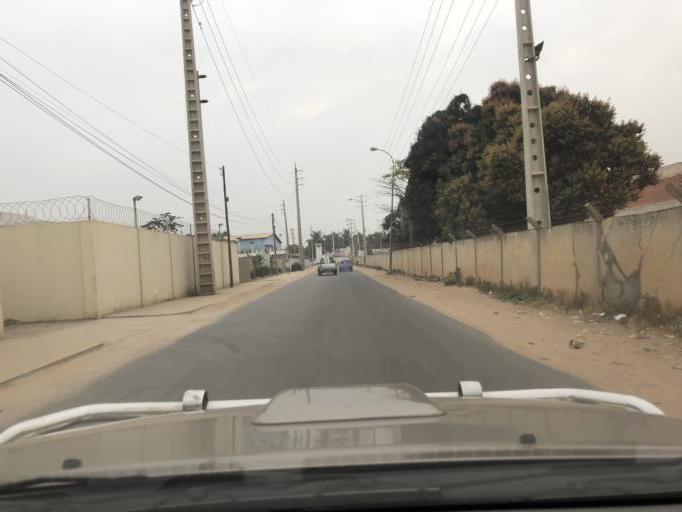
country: AO
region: Luanda
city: Luanda
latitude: -8.8893
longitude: 13.1894
